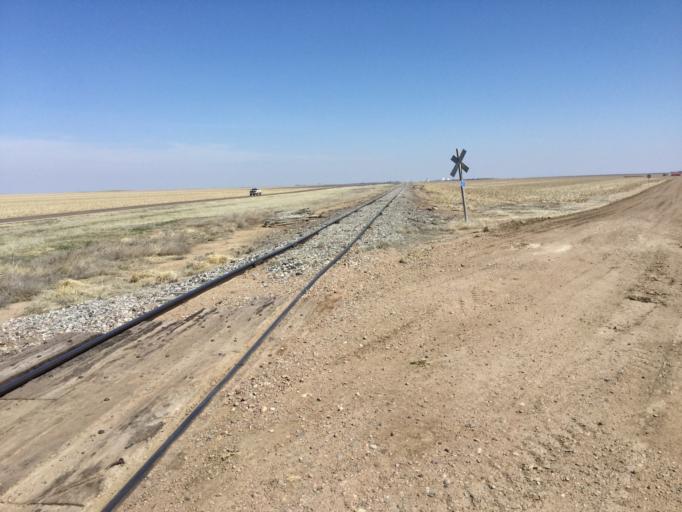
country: US
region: Kansas
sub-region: Stanton County
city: Johnson
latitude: 37.5344
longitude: -101.8482
